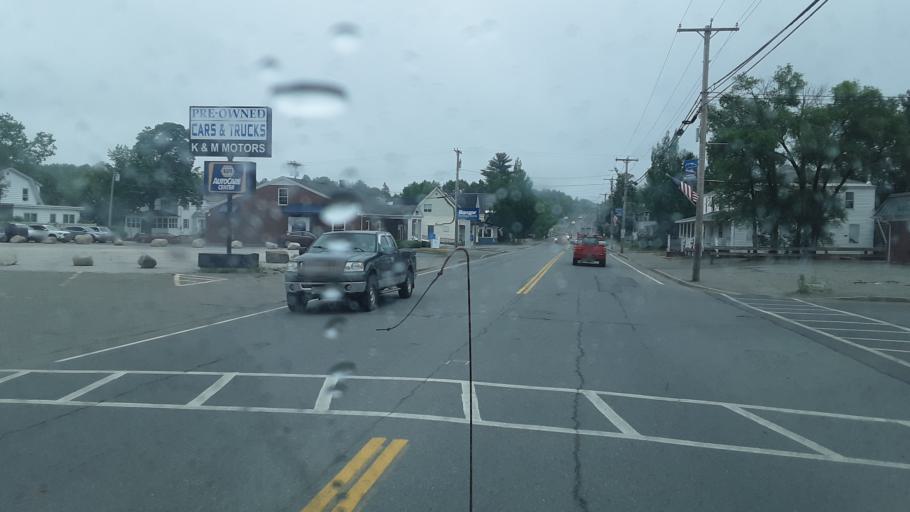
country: US
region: Maine
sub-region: Penobscot County
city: Millinocket
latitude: 45.6573
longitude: -68.7083
